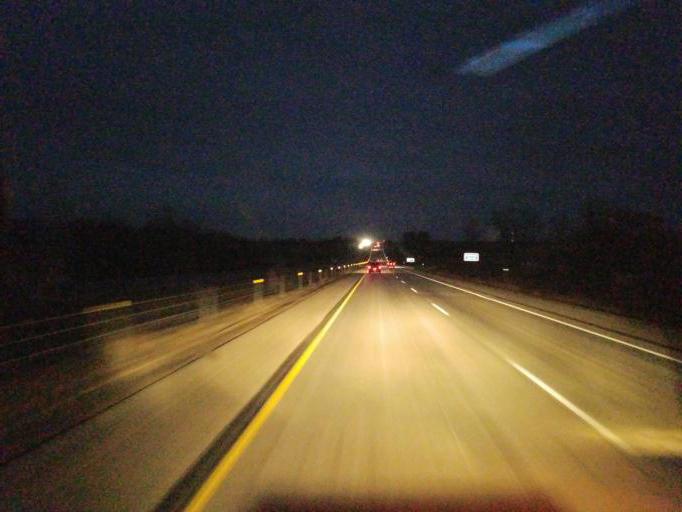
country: US
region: Iowa
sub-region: Guthrie County
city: Guthrie Center
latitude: 41.4964
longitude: -94.5401
